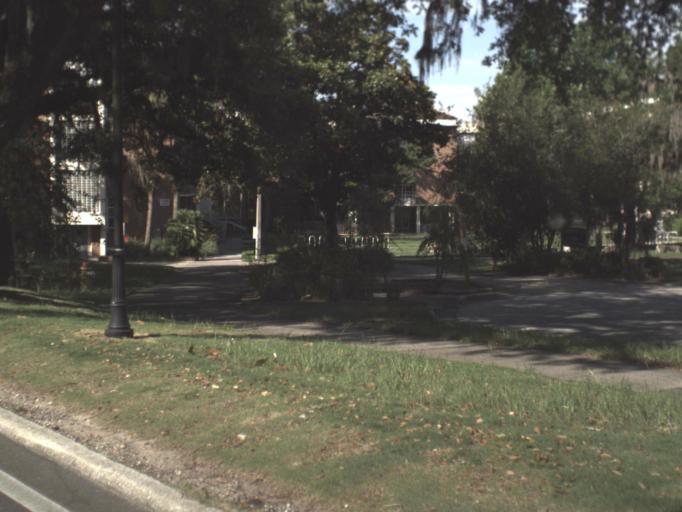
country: US
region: Florida
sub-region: Alachua County
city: Gainesville
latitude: 29.6473
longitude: -82.3394
